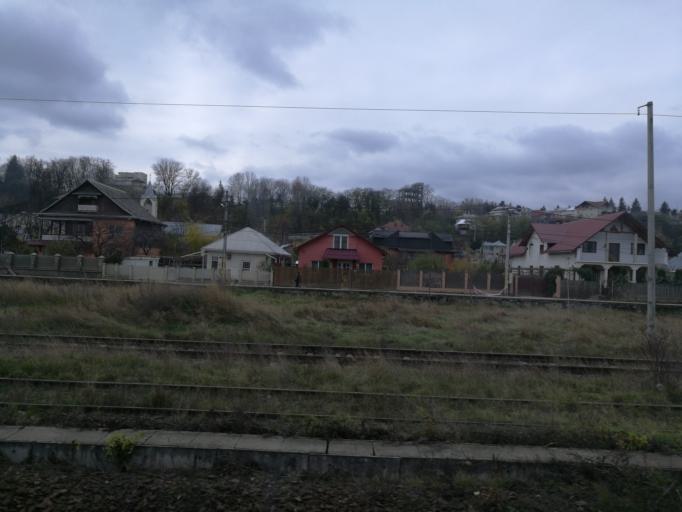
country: RO
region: Iasi
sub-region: Municipiul Pascani
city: Pascani
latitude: 47.2478
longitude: 26.7296
